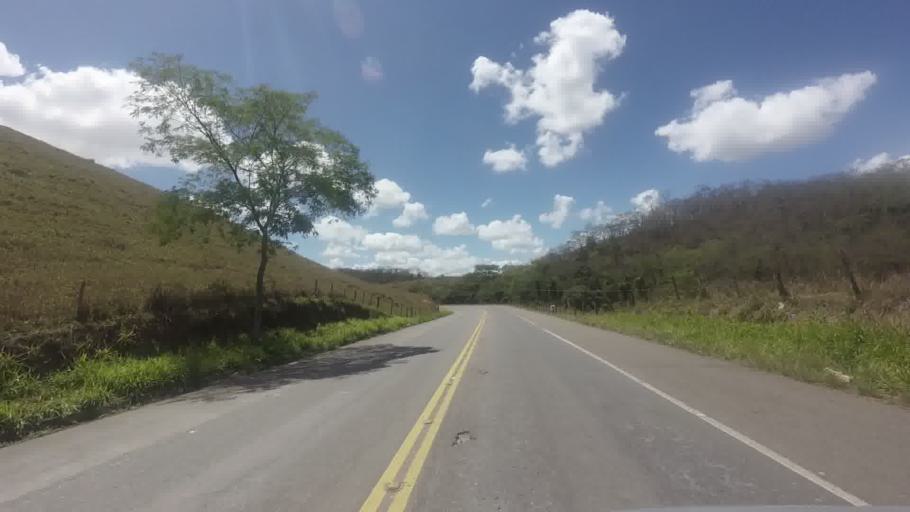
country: BR
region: Rio de Janeiro
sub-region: Santo Antonio De Padua
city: Santo Antonio de Padua
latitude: -21.6585
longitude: -42.3206
